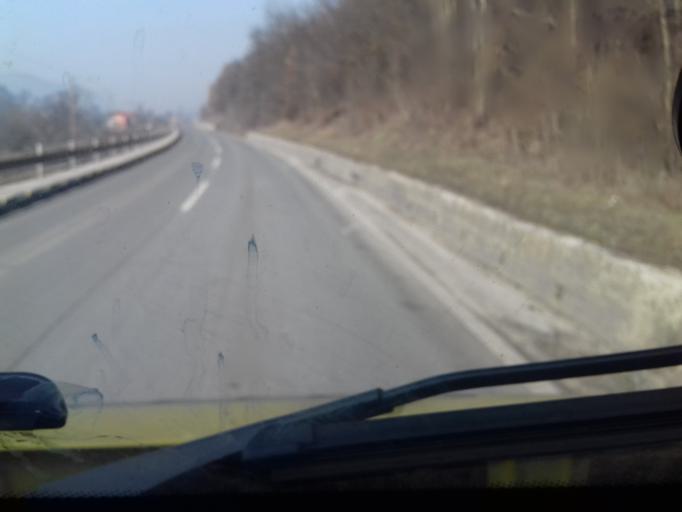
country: BA
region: Federation of Bosnia and Herzegovina
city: Vogosca
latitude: 43.9086
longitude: 18.3268
